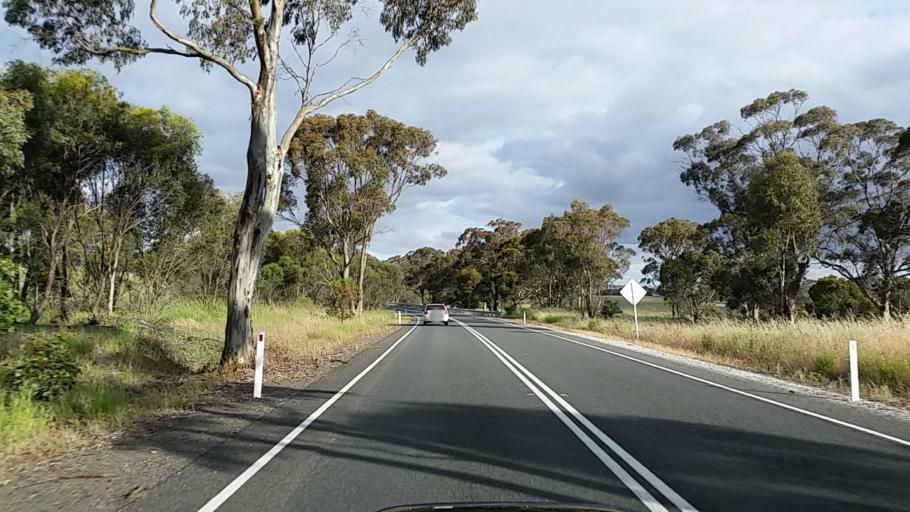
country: AU
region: South Australia
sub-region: Barossa
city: Angaston
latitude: -34.5719
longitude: 139.1565
